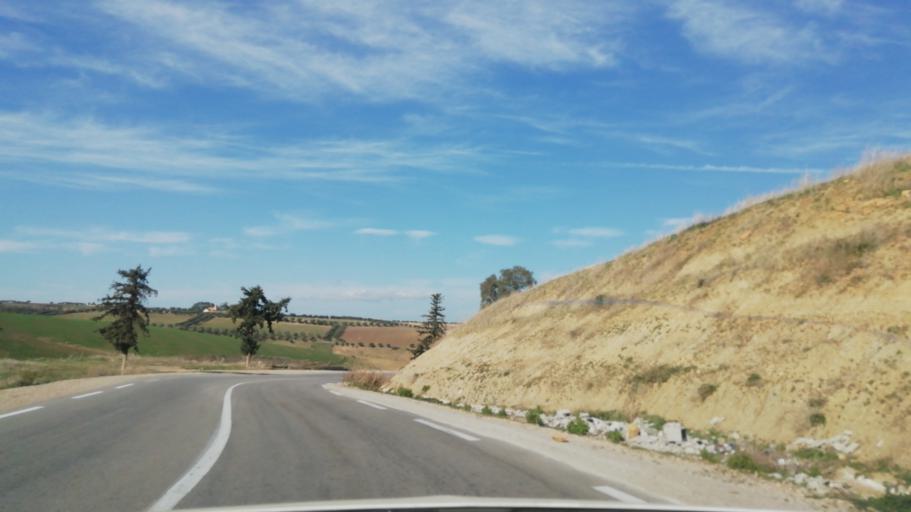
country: DZ
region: Tlemcen
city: Chetouane
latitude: 34.9657
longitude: -1.2465
